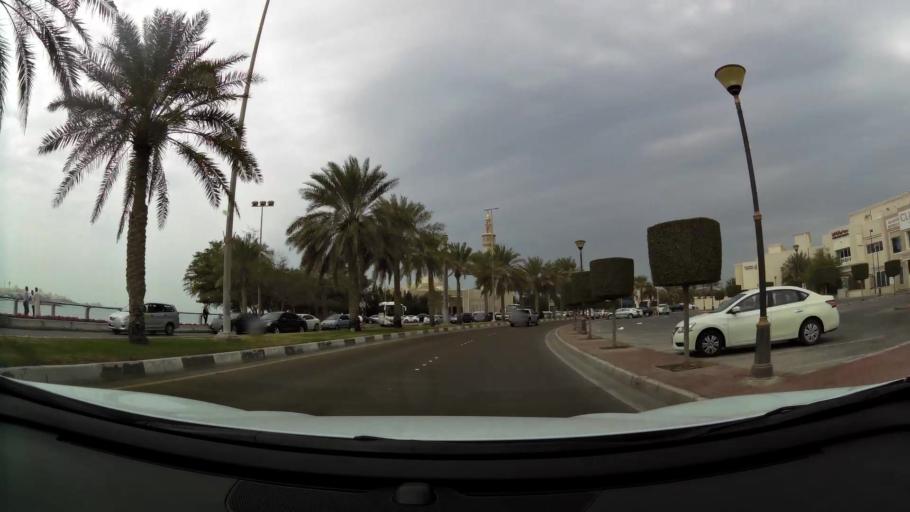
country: AE
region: Abu Dhabi
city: Abu Dhabi
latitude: 24.4724
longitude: 54.3177
